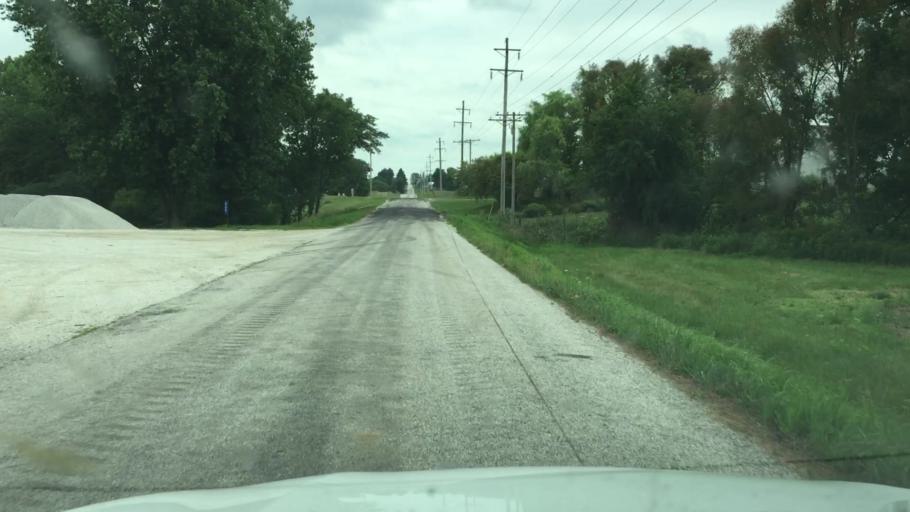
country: US
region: Illinois
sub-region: Hancock County
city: Carthage
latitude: 40.3318
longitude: -91.0825
